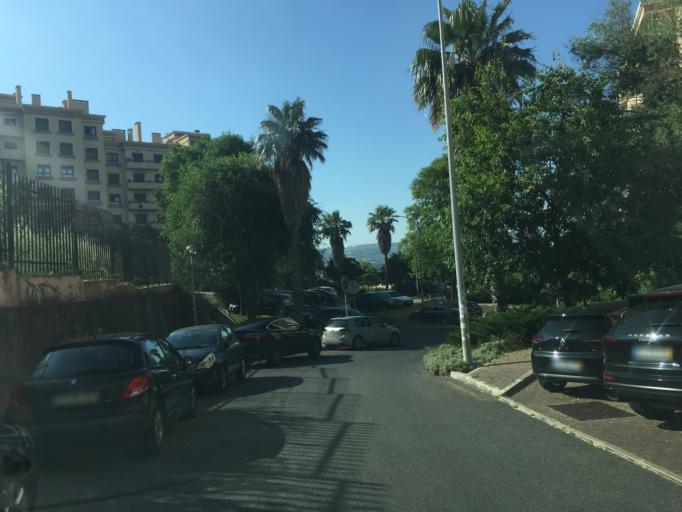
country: PT
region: Lisbon
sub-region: Loures
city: Loures
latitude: 38.8168
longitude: -9.1581
